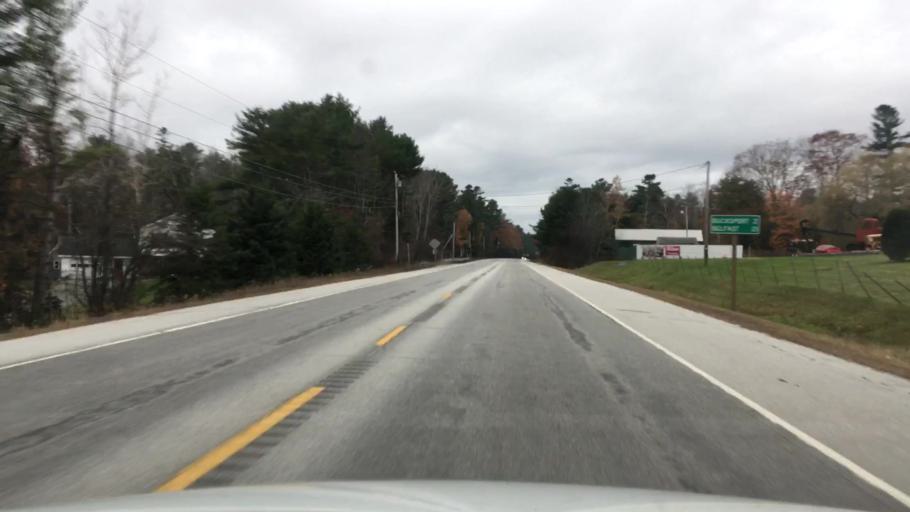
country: US
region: Maine
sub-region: Hancock County
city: Orland
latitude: 44.5722
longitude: -68.7554
